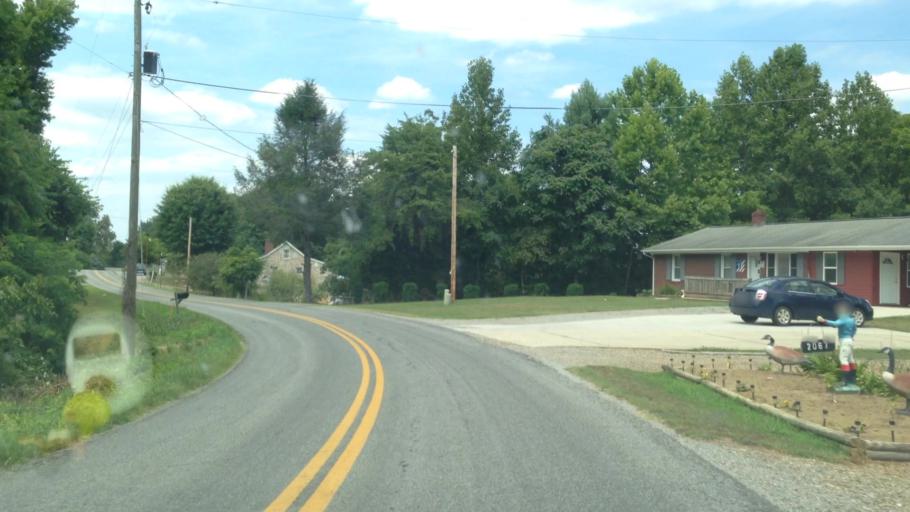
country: US
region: Virginia
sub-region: Henry County
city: Chatmoss
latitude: 36.6034
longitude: -79.8504
